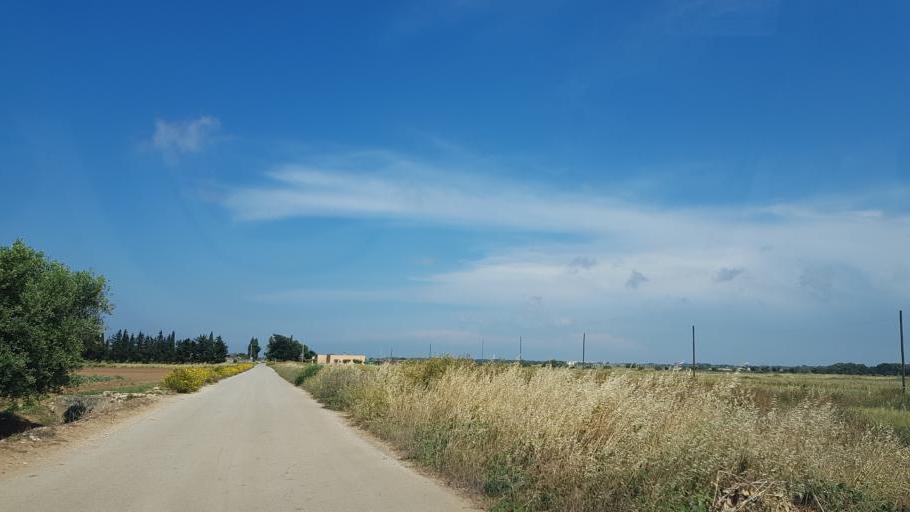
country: IT
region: Apulia
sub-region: Provincia di Brindisi
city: Brindisi
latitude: 40.6603
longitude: 17.8536
